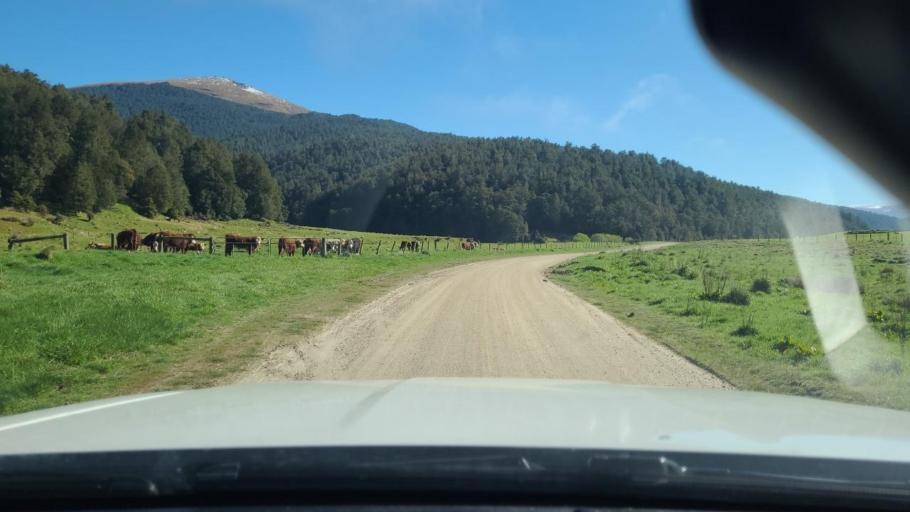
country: NZ
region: Otago
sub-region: Queenstown-Lakes District
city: Kingston
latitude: -45.5721
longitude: 169.0043
